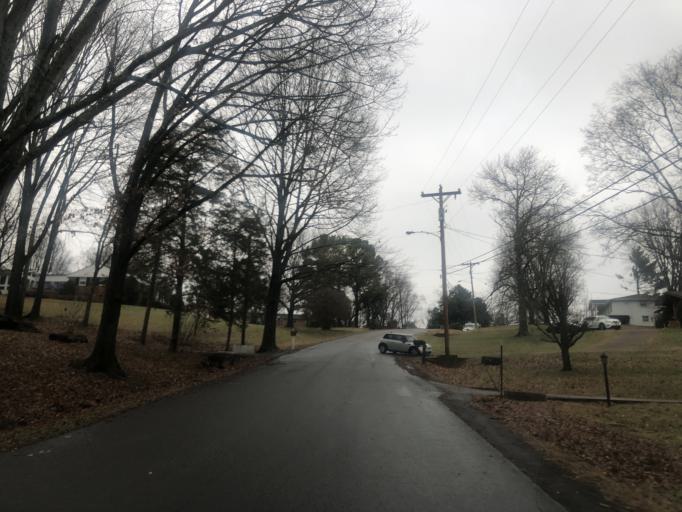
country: US
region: Tennessee
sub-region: Davidson County
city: Nashville
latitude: 36.1651
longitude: -86.6922
